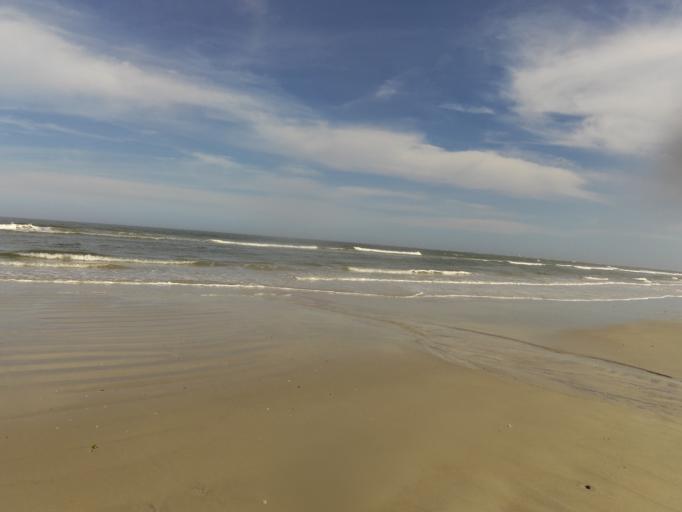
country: US
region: Florida
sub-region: Saint Johns County
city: Villano Beach
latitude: 29.9241
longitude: -81.2928
